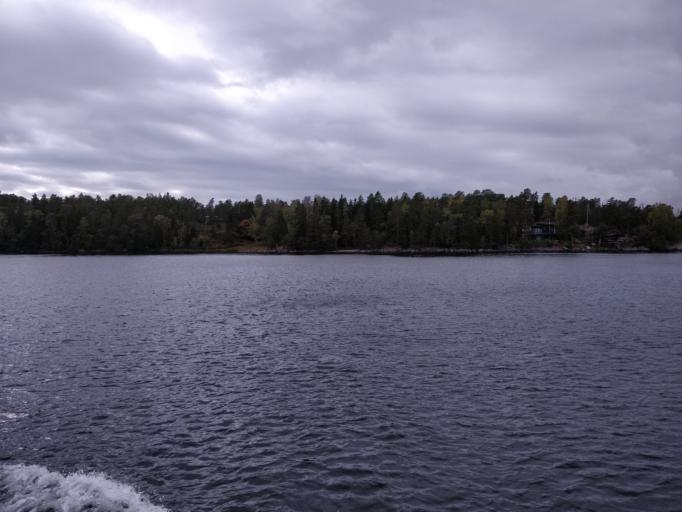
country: FI
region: Uusimaa
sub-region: Helsinki
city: Vantaa
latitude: 60.1686
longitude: 25.0971
